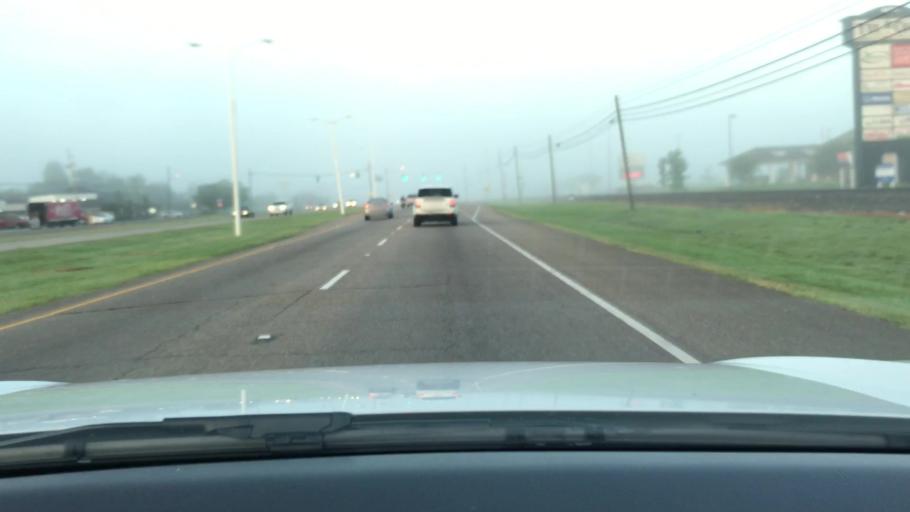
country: US
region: Louisiana
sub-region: West Baton Rouge Parish
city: Brusly
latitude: 30.3879
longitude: -91.2441
